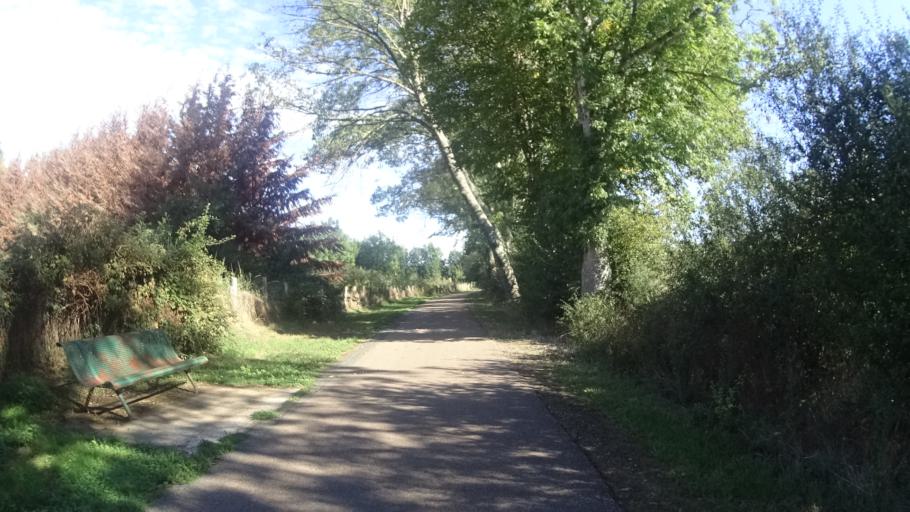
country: FR
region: Centre
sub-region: Departement du Cher
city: Saint-Satur
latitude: 47.3331
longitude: 2.8626
